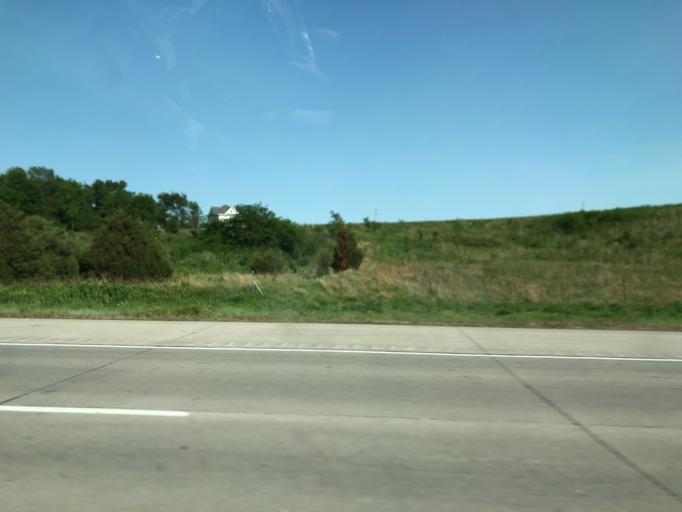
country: US
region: Nebraska
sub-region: Saunders County
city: Ashland
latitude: 40.9581
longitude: -96.4090
